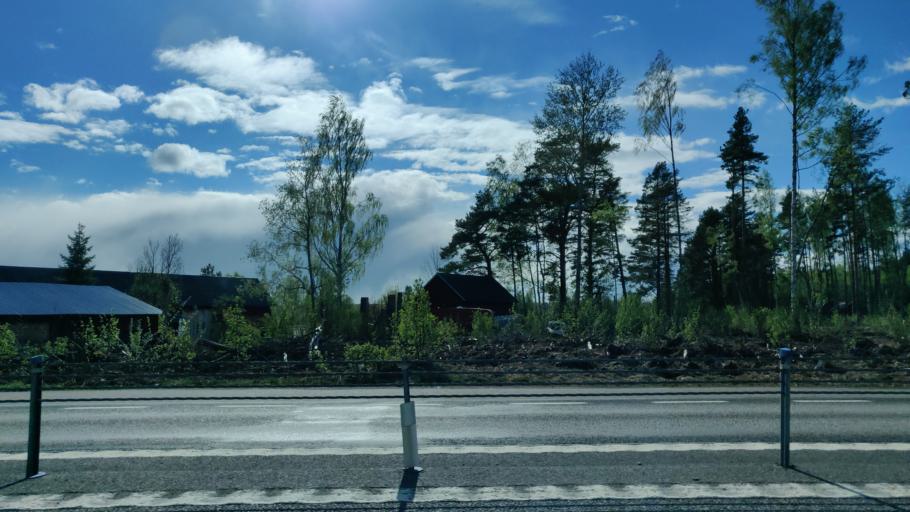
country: SE
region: Vaermland
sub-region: Forshaga Kommun
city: Forshaga
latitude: 59.4650
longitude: 13.4155
